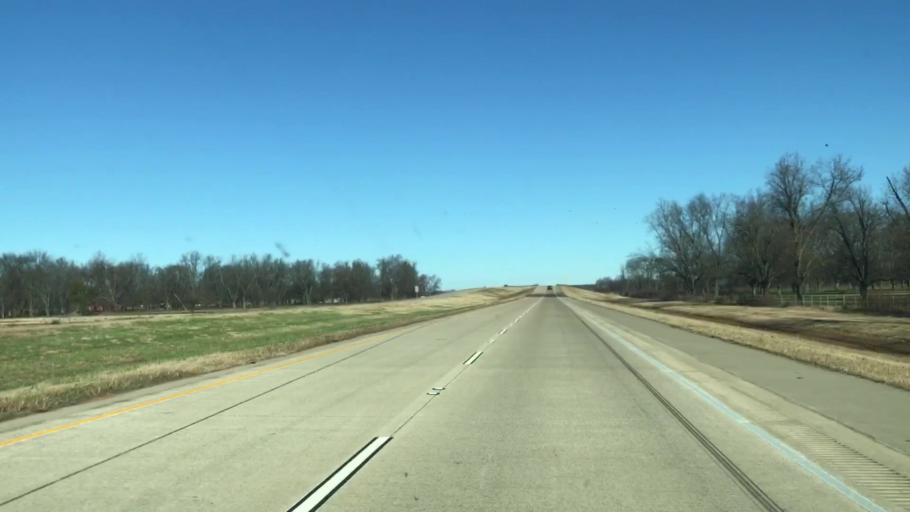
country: US
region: Louisiana
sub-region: Caddo Parish
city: Oil City
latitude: 32.7407
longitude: -93.8775
